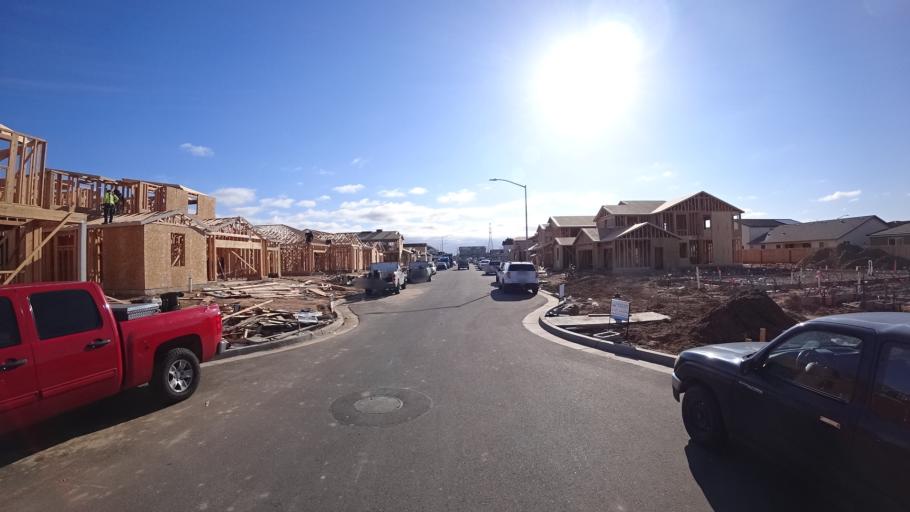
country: US
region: California
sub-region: Fresno County
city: West Park
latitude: 36.8040
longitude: -119.9051
